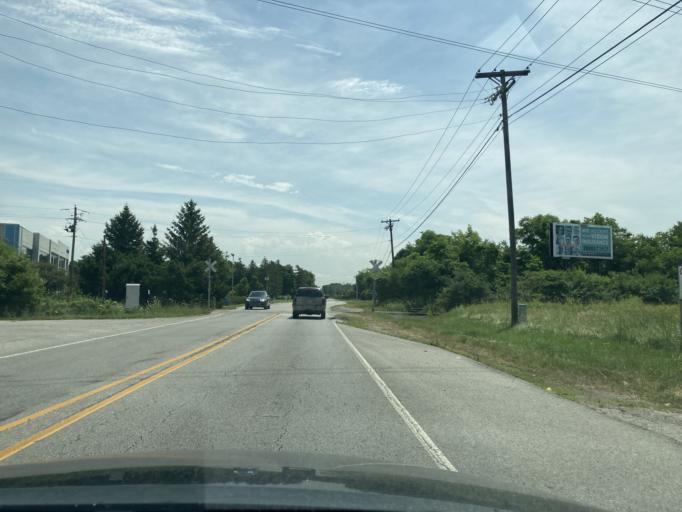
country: US
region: Indiana
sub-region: Marion County
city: Speedway
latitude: 39.8677
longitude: -86.2301
